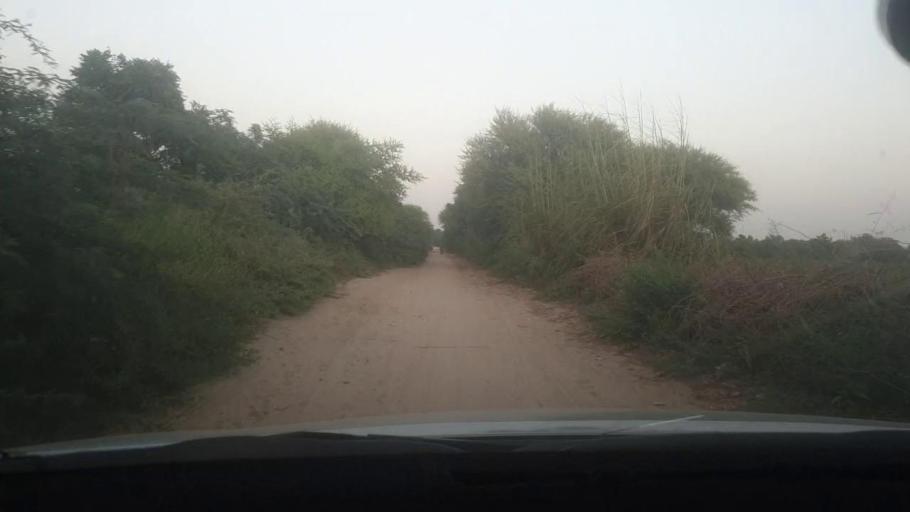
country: PK
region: Sindh
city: Pithoro
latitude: 25.7350
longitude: 69.4816
